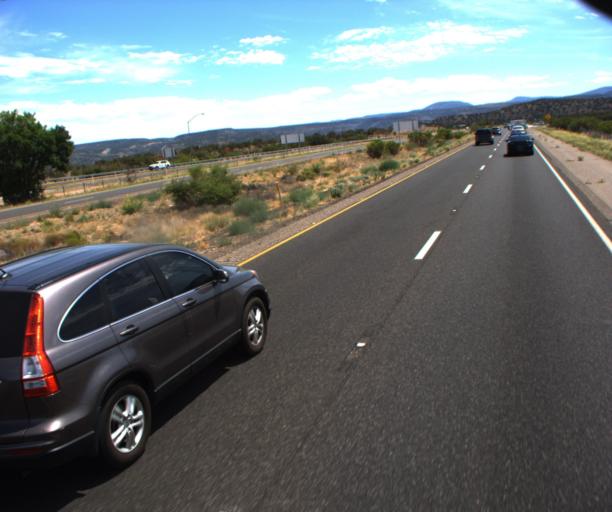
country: US
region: Arizona
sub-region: Yavapai County
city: Lake Montezuma
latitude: 34.6733
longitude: -111.7718
